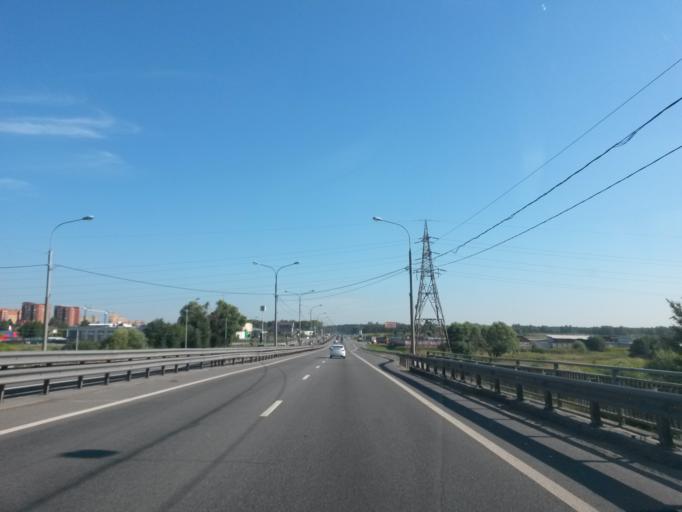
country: RU
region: Moskovskaya
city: Lesnyye Polyany
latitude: 55.9899
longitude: 37.8729
